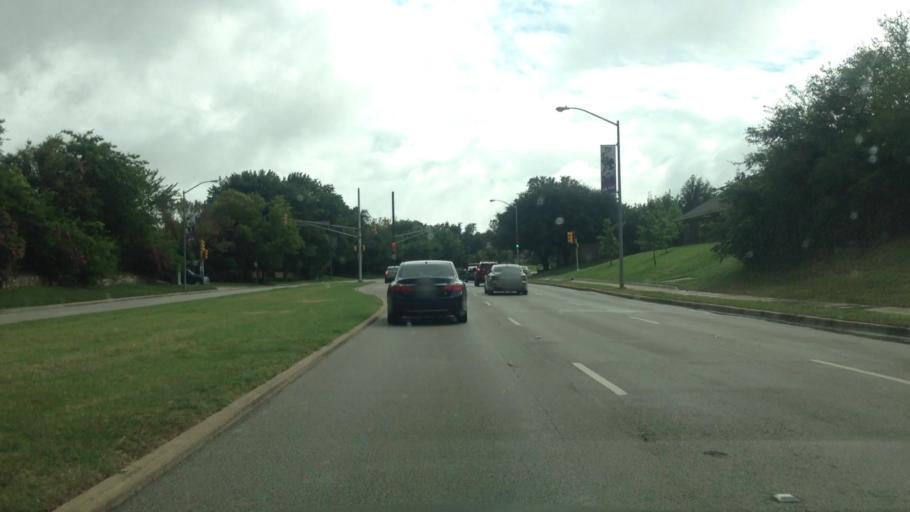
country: US
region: Texas
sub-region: Tarrant County
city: Edgecliff Village
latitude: 32.6970
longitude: -97.3908
